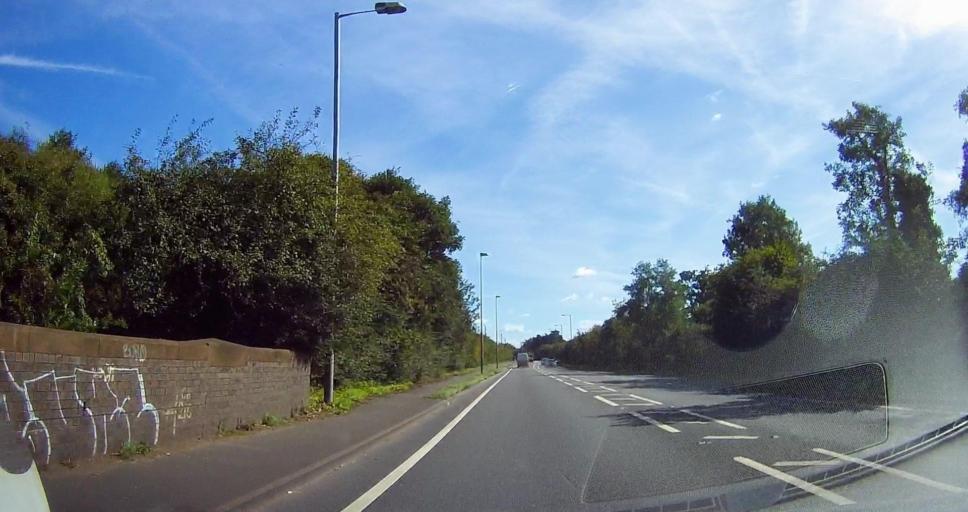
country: GB
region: England
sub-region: Staffordshire
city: Great Wyrley
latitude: 52.6708
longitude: -2.0163
